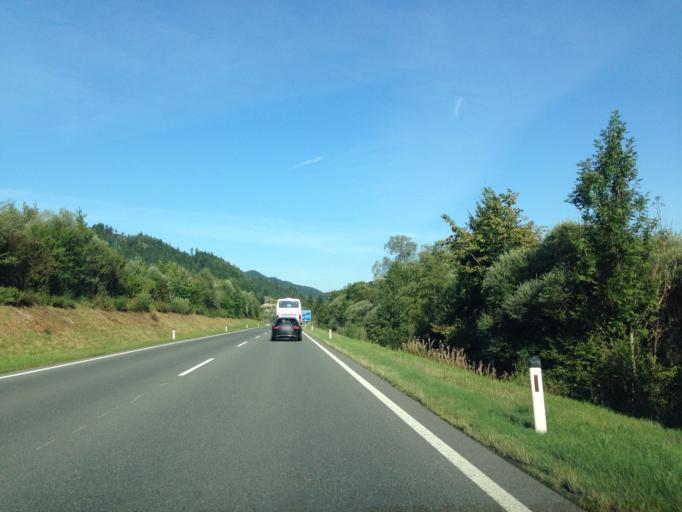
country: AT
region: Tyrol
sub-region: Politischer Bezirk Reutte
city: Musau
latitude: 47.5364
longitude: 10.6742
